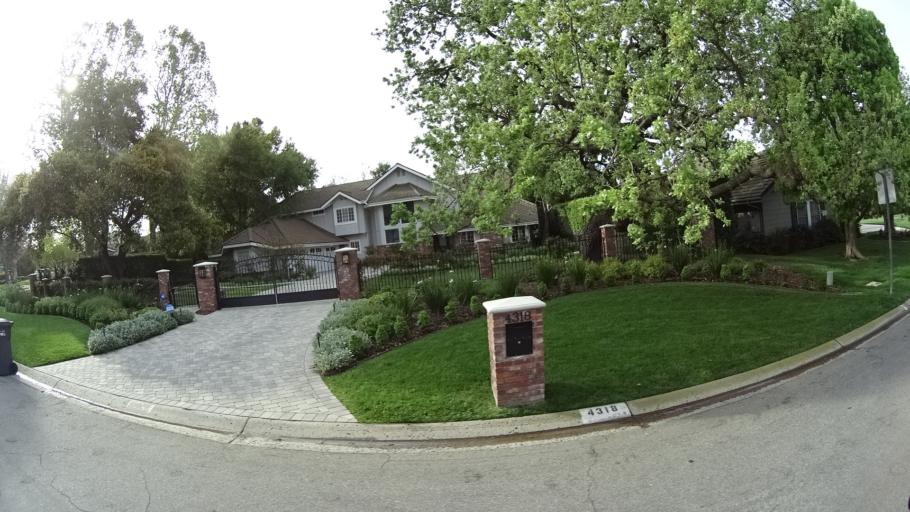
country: US
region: California
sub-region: Ventura County
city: Thousand Oaks
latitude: 34.1960
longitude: -118.8164
